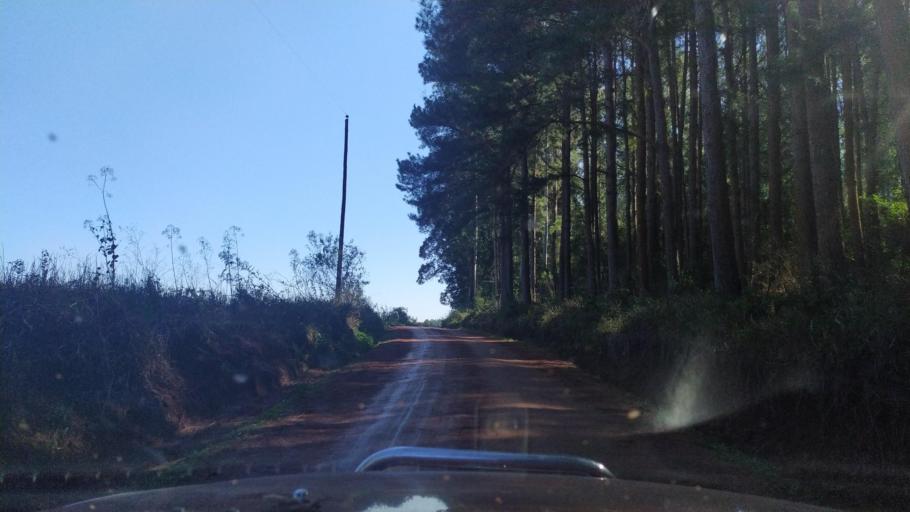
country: AR
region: Misiones
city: El Alcazar
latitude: -26.7339
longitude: -54.6590
